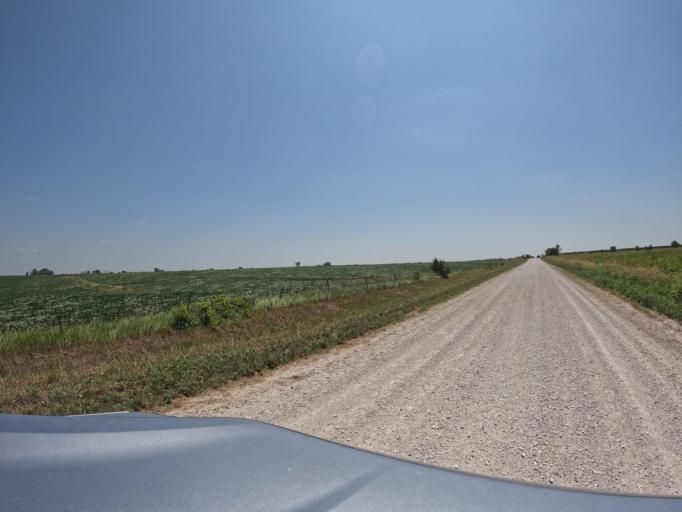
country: US
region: Iowa
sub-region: Keokuk County
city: Sigourney
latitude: 41.2702
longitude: -92.1806
